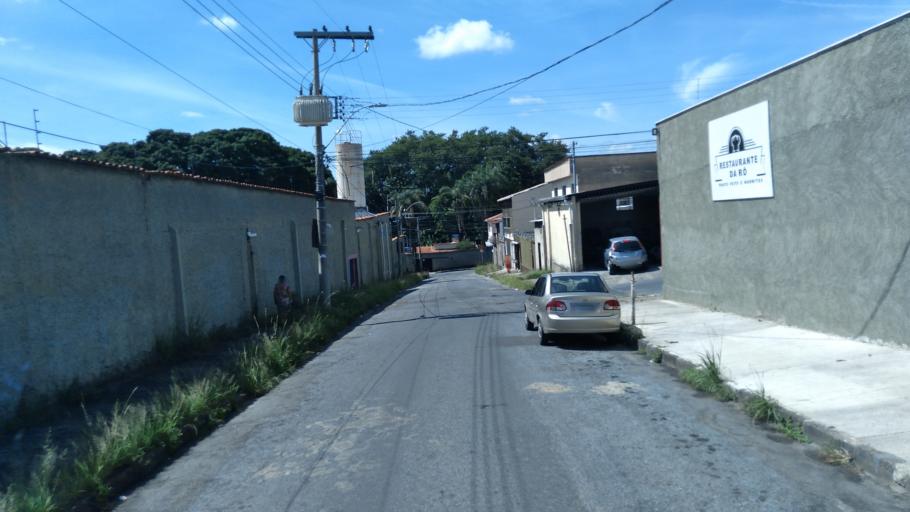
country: BR
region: Minas Gerais
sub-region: Contagem
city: Contagem
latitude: -19.8921
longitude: -44.0106
